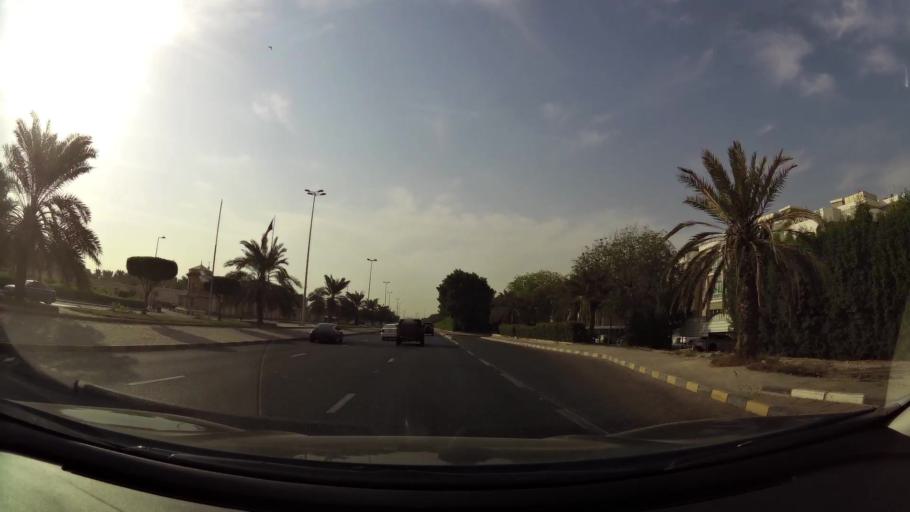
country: KW
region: Muhafazat Hawalli
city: Salwa
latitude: 29.2950
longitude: 48.0850
